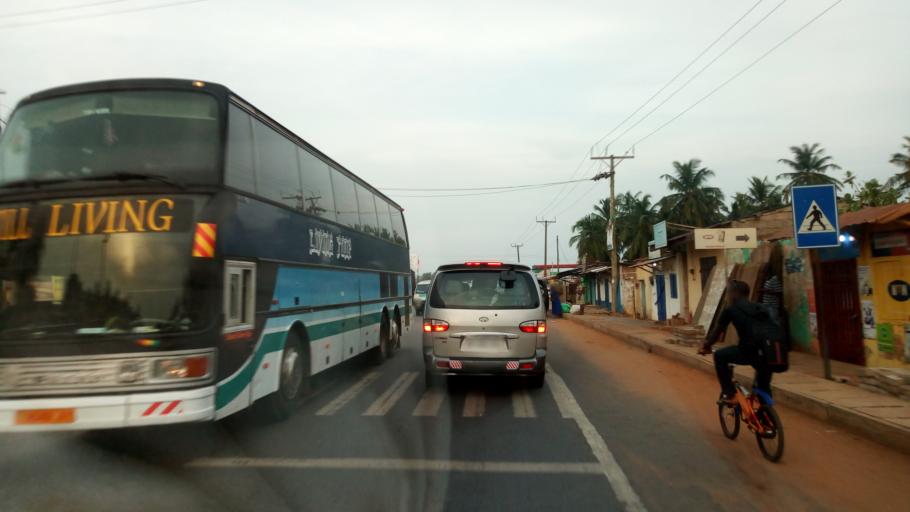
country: TG
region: Maritime
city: Lome
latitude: 6.1133
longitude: 1.1646
